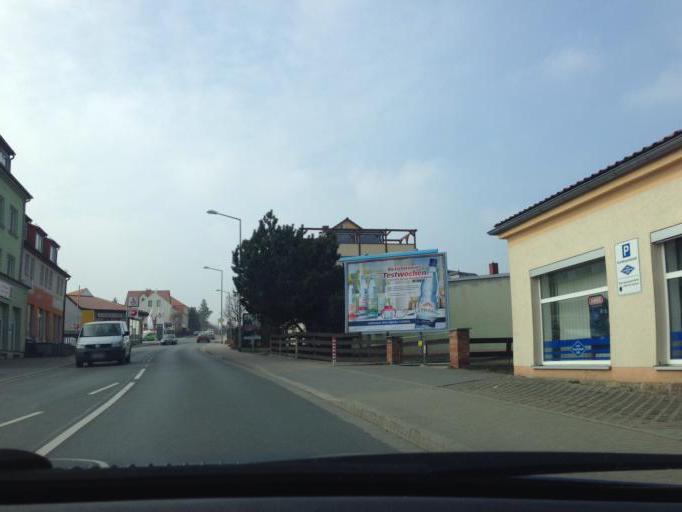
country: DE
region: Saxony
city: Freital
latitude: 51.0190
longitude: 13.6374
